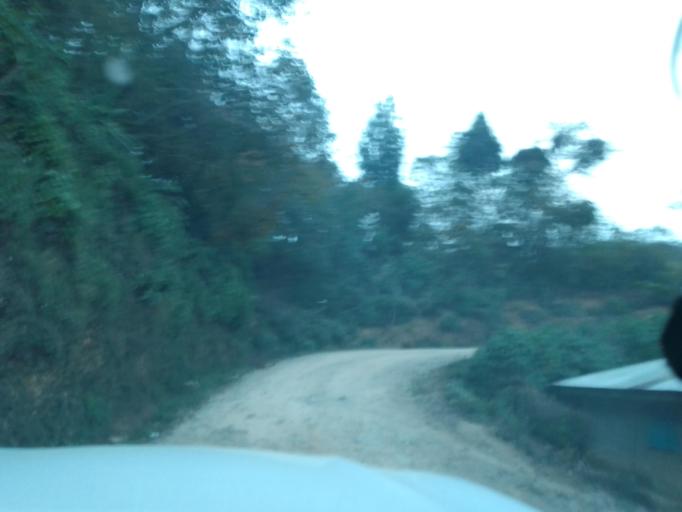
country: MX
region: Chiapas
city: Motozintla de Mendoza
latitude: 15.2151
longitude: -92.2343
